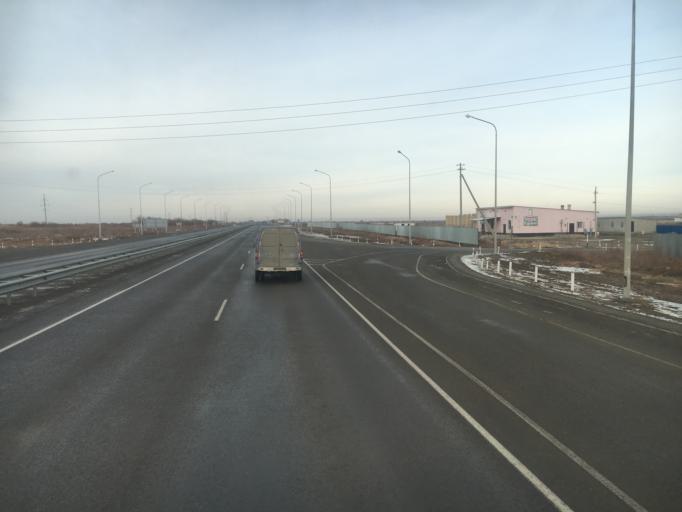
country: KZ
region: Qyzylorda
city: Shieli
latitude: 44.1398
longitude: 66.9650
